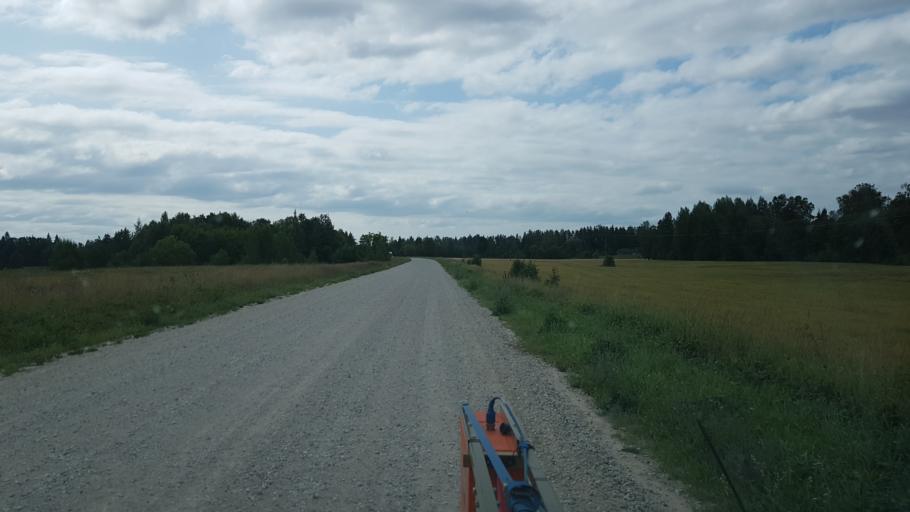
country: EE
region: Paernumaa
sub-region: Halinga vald
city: Parnu-Jaagupi
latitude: 58.5838
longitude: 24.4063
